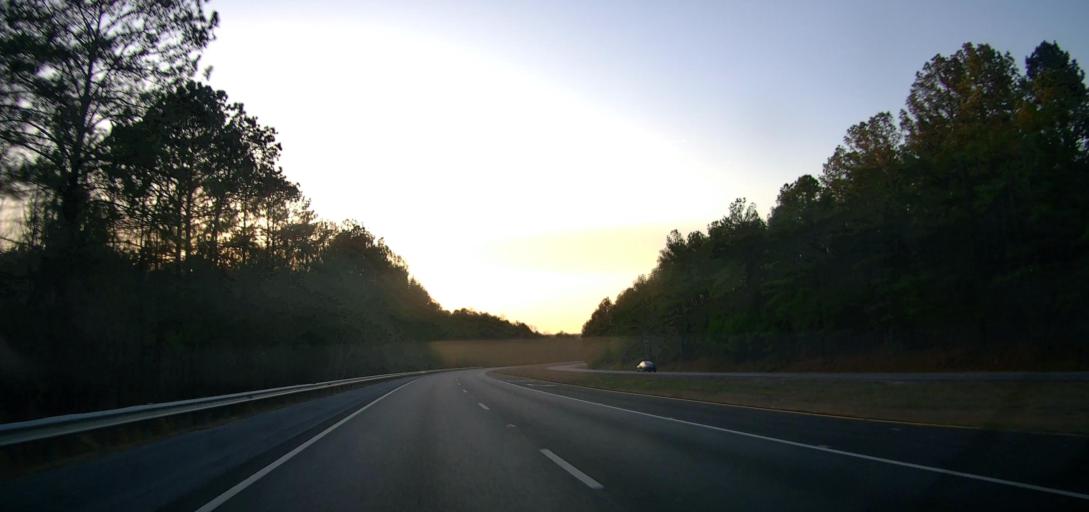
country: US
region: Alabama
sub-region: Coosa County
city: Stewartville
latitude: 33.0826
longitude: -86.1951
